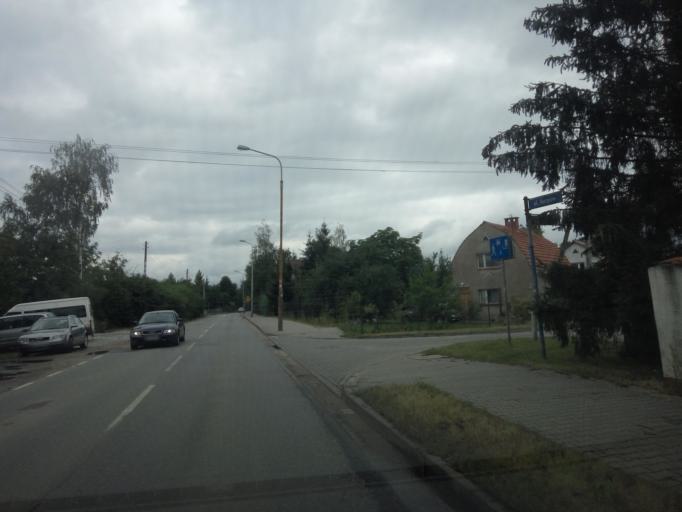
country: PL
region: Lower Silesian Voivodeship
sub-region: Powiat wroclawski
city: Zerniki Wroclawskie
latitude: 51.0506
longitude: 17.0300
